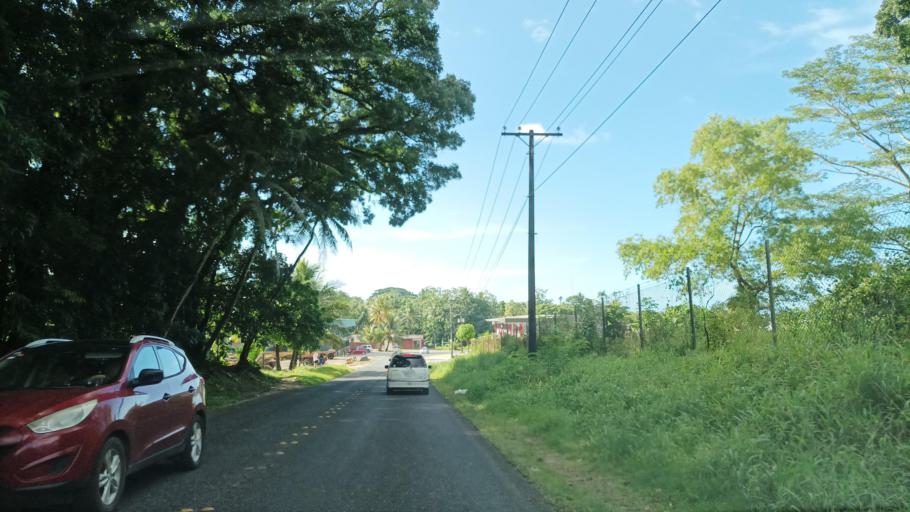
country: FM
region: Pohnpei
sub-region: Kolonia Municipality
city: Kolonia
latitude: 6.9585
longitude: 158.2155
